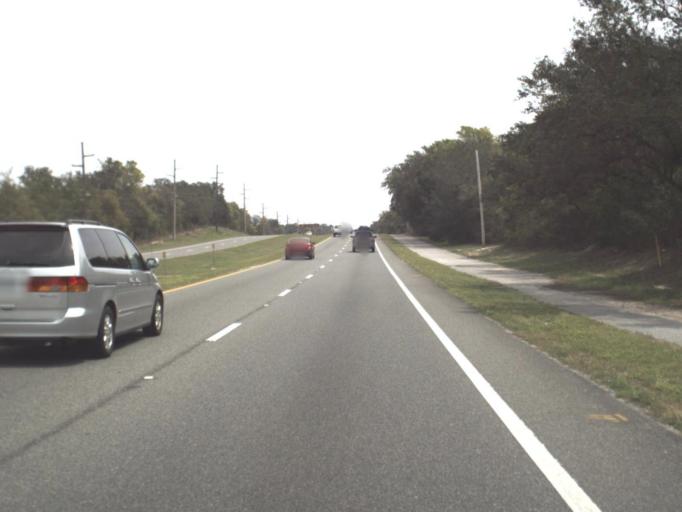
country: US
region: Florida
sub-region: Santa Rosa County
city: Gulf Breeze
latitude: 30.3622
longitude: -87.1422
